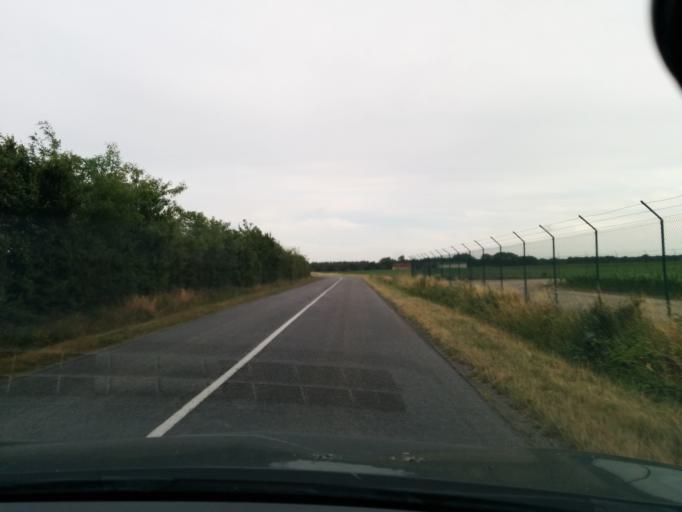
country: FR
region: Centre
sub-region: Departement du Loiret
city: Fay-aux-Loges
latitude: 47.9040
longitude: 2.1778
